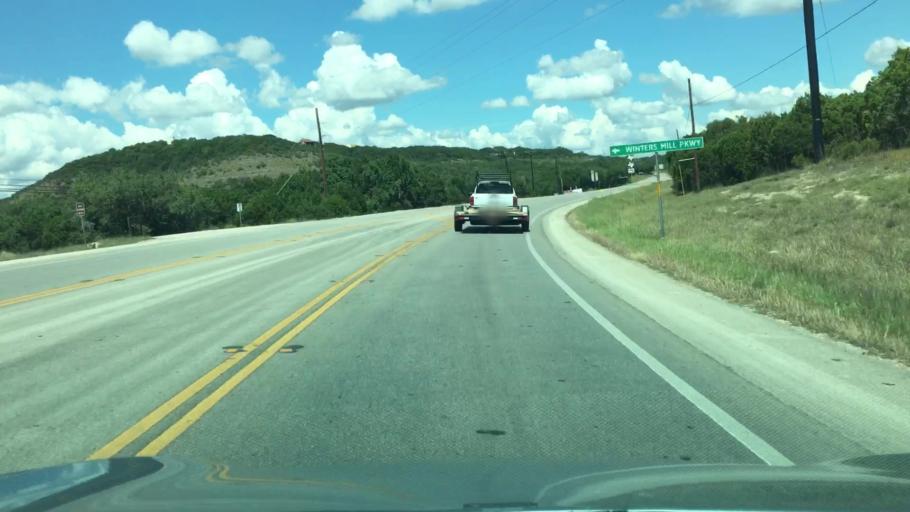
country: US
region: Texas
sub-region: Hays County
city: Wimberley
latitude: 30.0053
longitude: -98.0818
